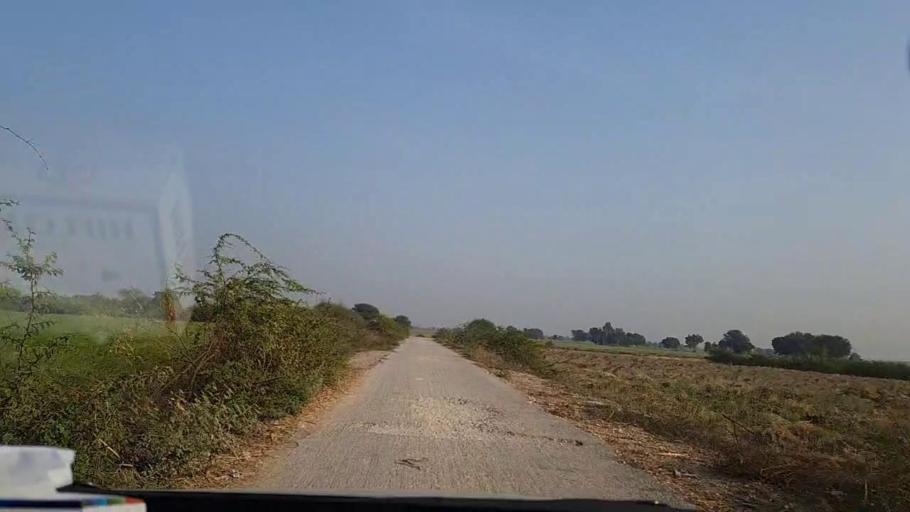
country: PK
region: Sindh
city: Tando Ghulam Ali
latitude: 25.2137
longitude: 68.8855
